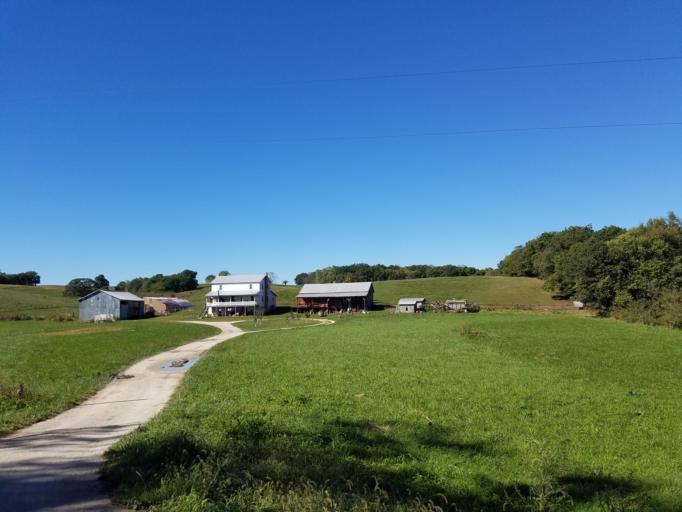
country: US
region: Iowa
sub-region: Decatur County
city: Lamoni
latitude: 40.6163
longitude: -93.8438
